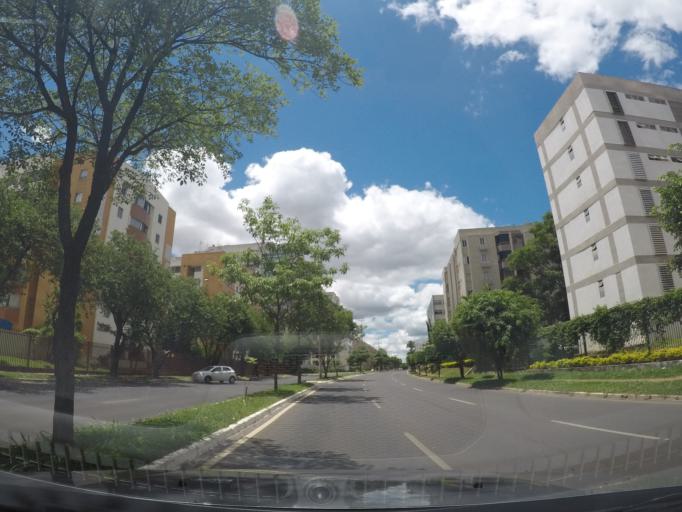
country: BR
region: Federal District
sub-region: Brasilia
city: Brasilia
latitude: -15.8387
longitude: -47.9781
